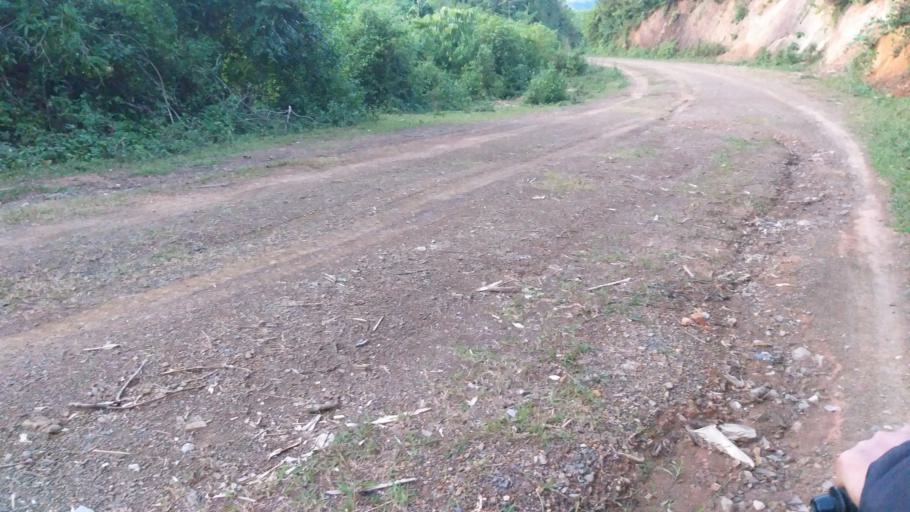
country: LA
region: Phongsali
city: Khoa
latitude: 21.4342
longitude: 102.6249
